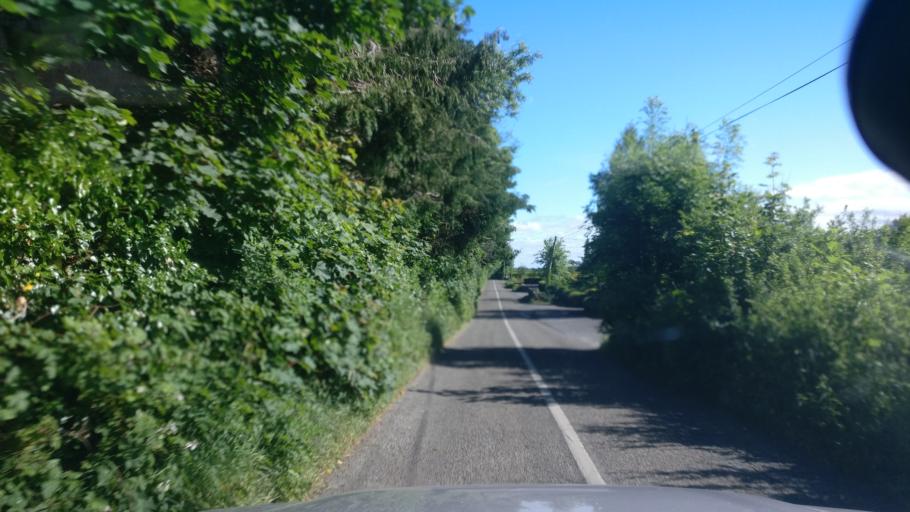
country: IE
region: Connaught
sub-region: County Galway
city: Loughrea
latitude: 53.2345
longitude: -8.6244
